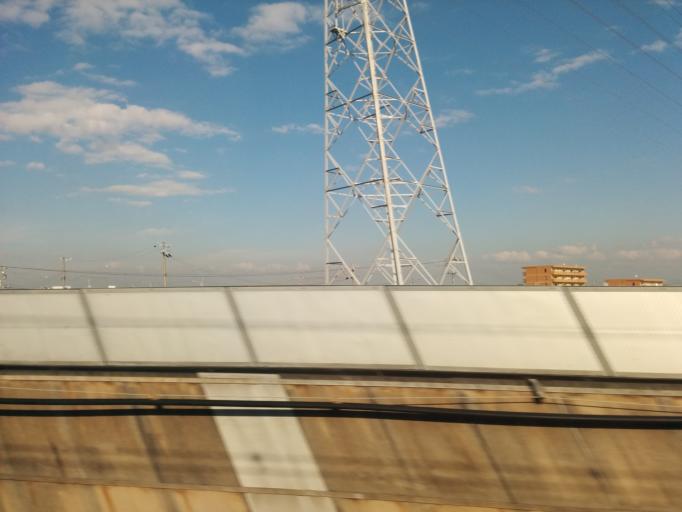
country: JP
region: Aichi
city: Chiryu
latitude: 34.9805
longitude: 137.0499
